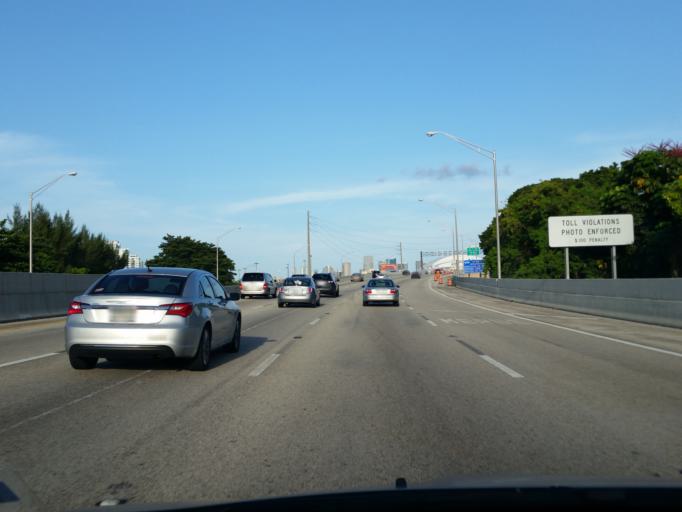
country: US
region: Florida
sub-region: Miami-Dade County
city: Allapattah
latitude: 25.7845
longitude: -80.2366
